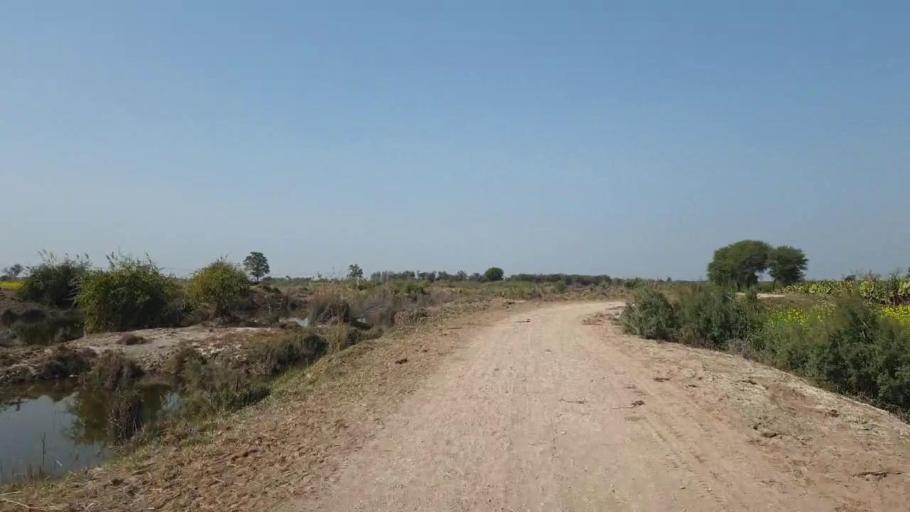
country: PK
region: Sindh
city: Hala
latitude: 25.9640
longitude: 68.4342
